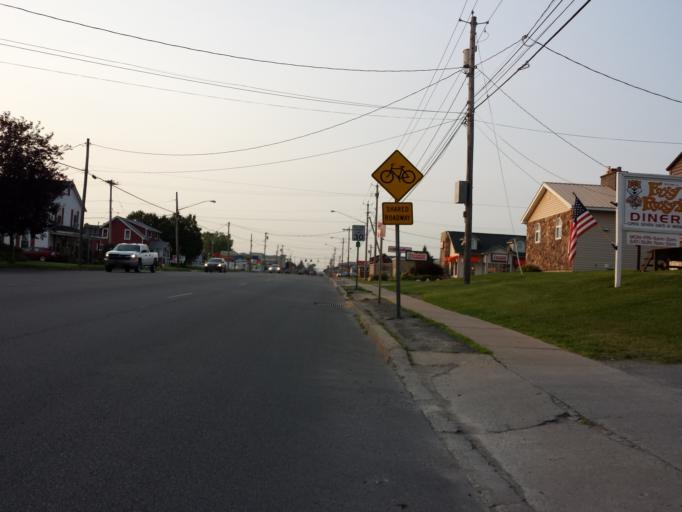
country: US
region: New York
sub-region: St. Lawrence County
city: Potsdam
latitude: 44.6784
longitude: -74.9868
